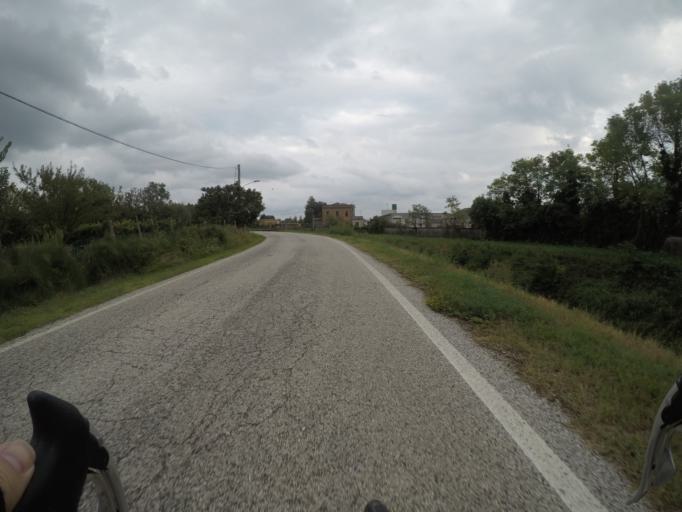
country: IT
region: Veneto
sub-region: Provincia di Rovigo
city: Polesella
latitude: 44.9613
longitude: 11.7344
